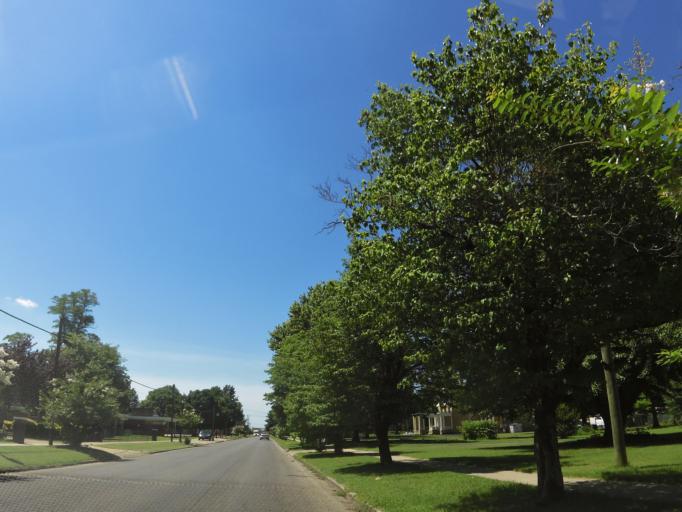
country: US
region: Missouri
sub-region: New Madrid County
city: New Madrid
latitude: 36.5924
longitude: -89.5273
